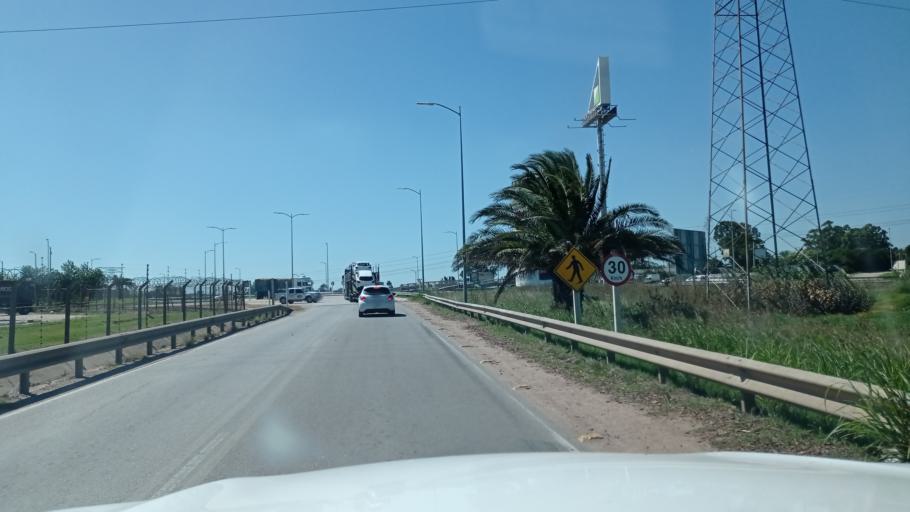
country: UY
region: Montevideo
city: Pajas Blancas
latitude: -34.8530
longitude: -56.2902
